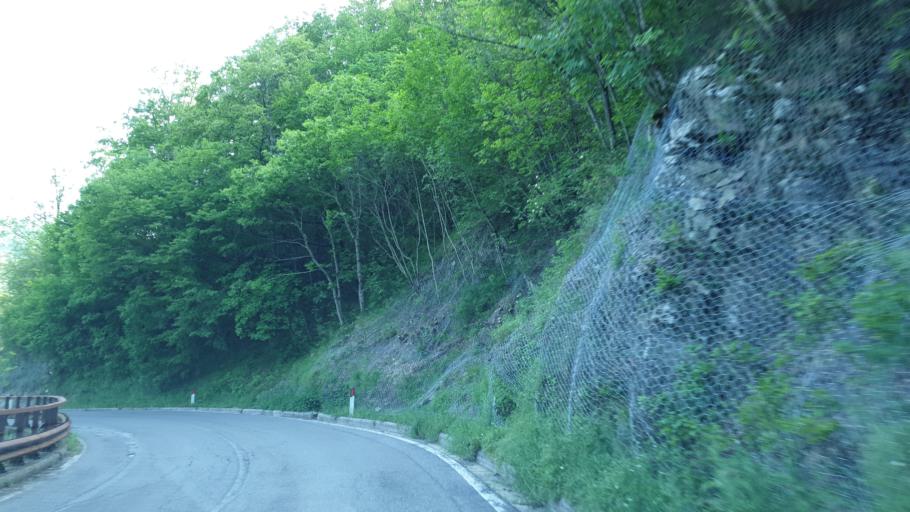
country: IT
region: Tuscany
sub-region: Province of Arezzo
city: Soci
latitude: 43.7759
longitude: 11.8684
